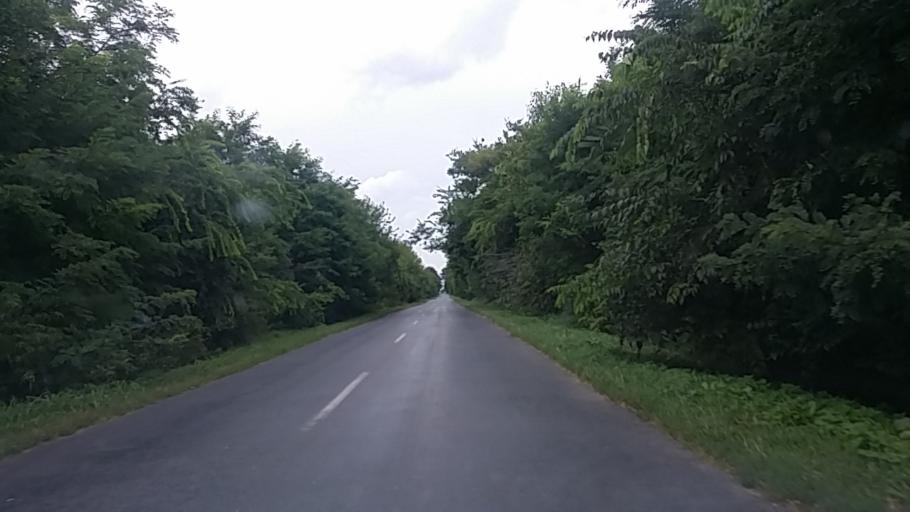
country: HU
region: Tolna
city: Szedres
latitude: 46.5282
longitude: 18.6453
